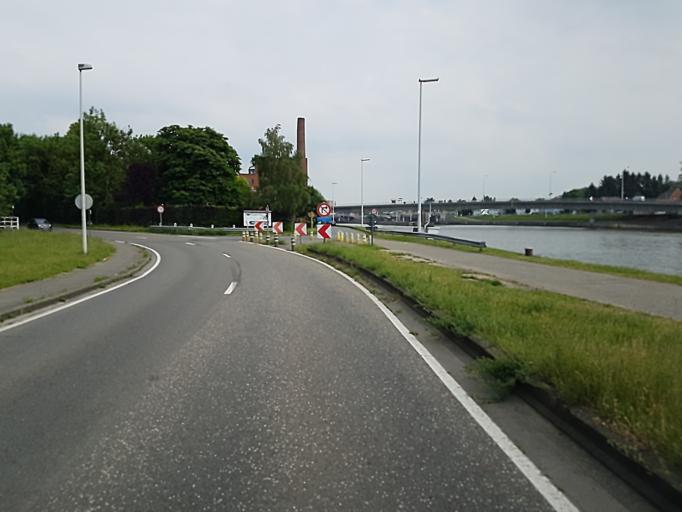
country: BE
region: Flanders
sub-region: Provincie Antwerpen
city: Wijnegem
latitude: 51.2297
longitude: 4.5308
